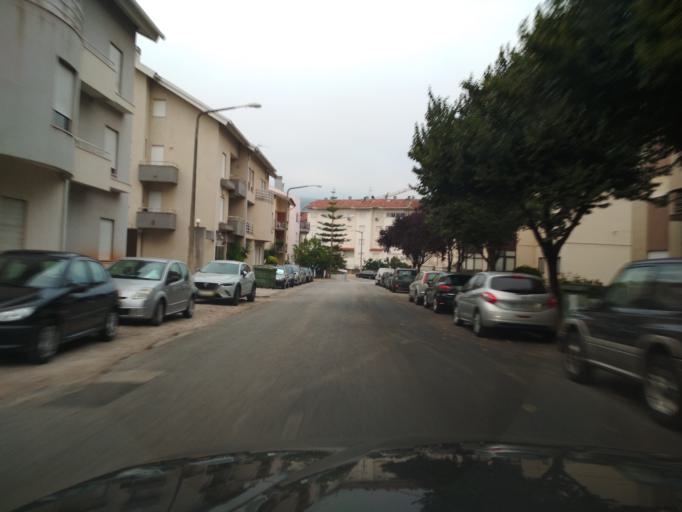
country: PT
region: Coimbra
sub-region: Coimbra
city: Coimbra
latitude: 40.1973
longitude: -8.4048
